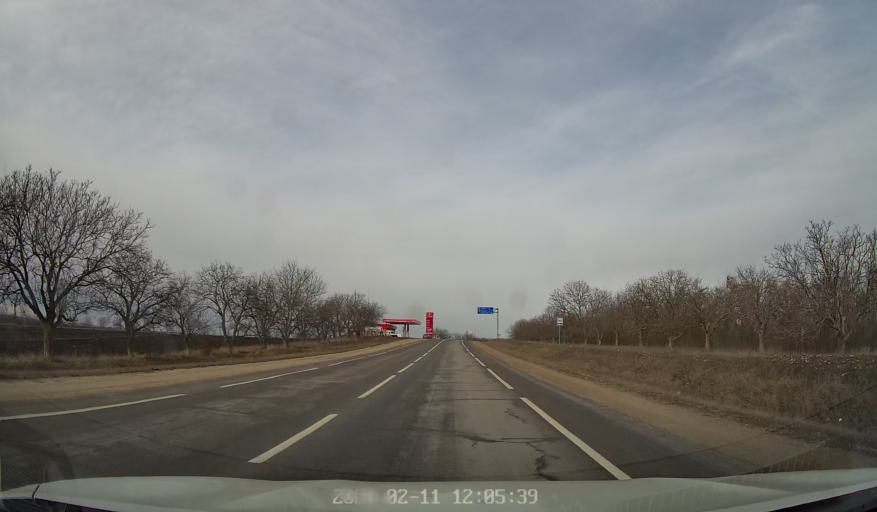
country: MD
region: Riscani
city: Riscani
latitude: 47.9844
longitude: 27.5790
